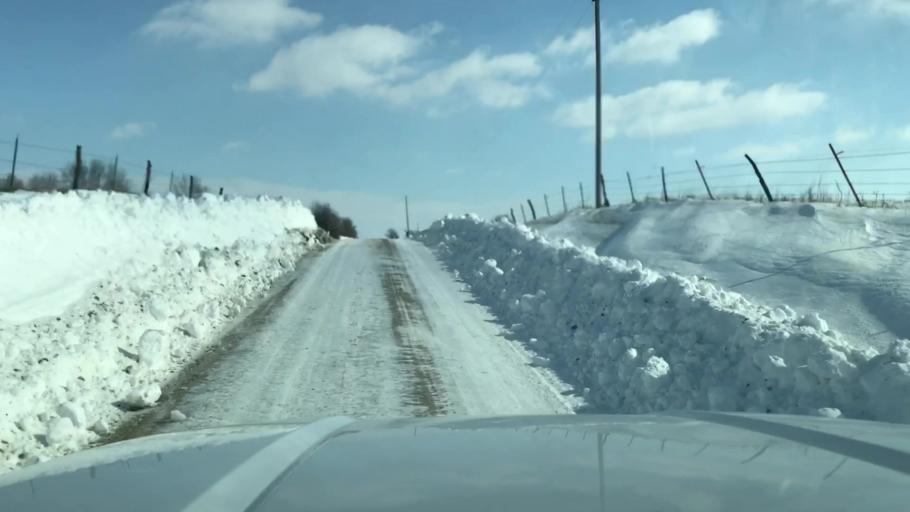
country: US
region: Missouri
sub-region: Nodaway County
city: Maryville
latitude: 40.3868
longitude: -94.7147
